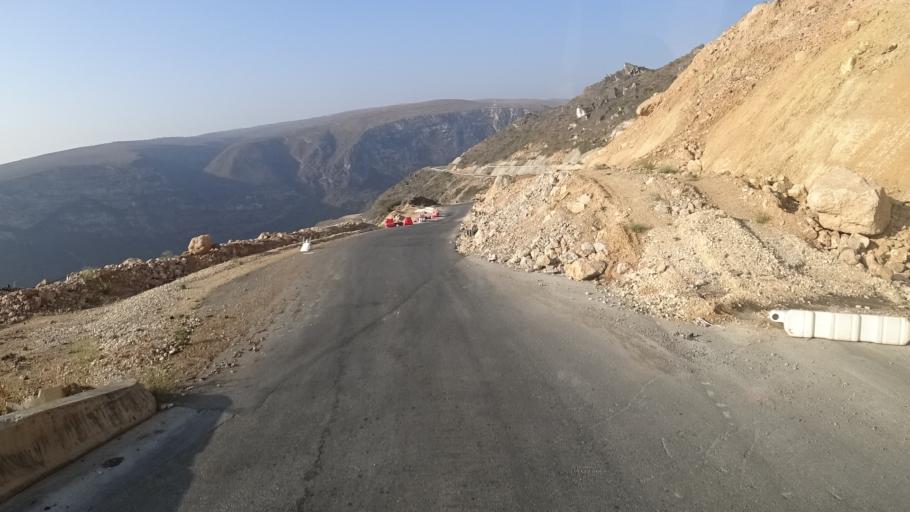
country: YE
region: Al Mahrah
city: Hawf
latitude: 16.7564
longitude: 53.2222
